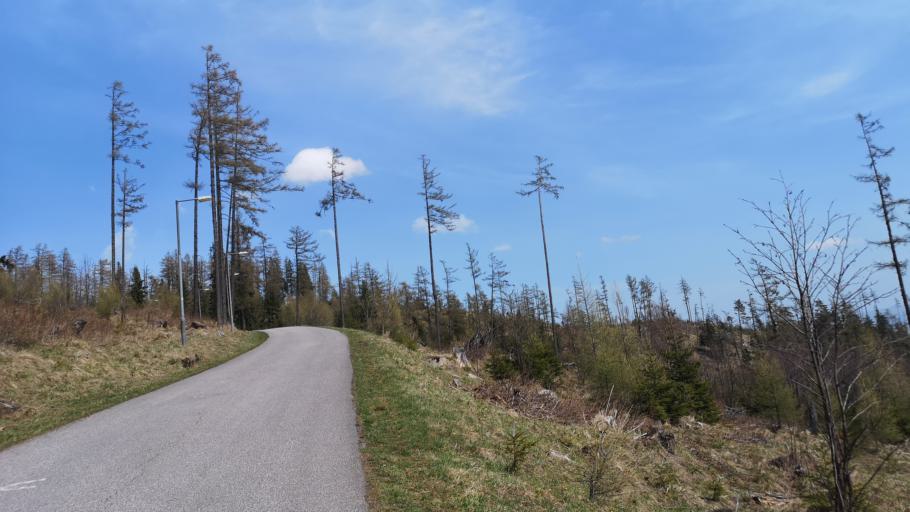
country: SK
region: Presovsky
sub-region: Okres Poprad
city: Vysoke Tatry
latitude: 49.1560
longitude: 20.2250
